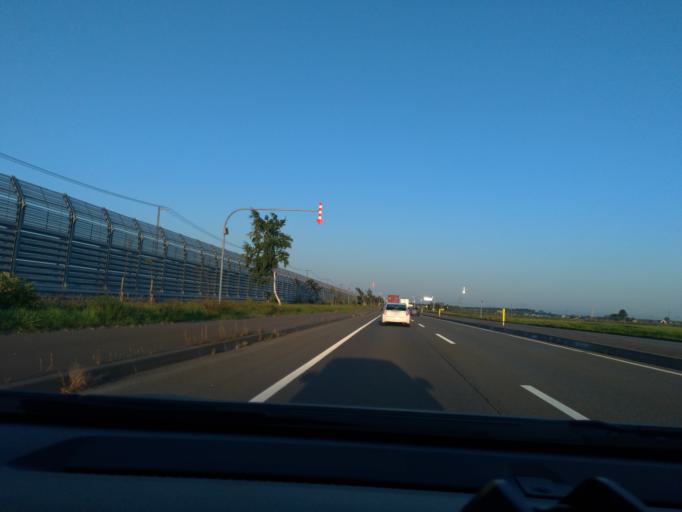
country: JP
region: Hokkaido
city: Tobetsu
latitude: 43.1789
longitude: 141.4584
